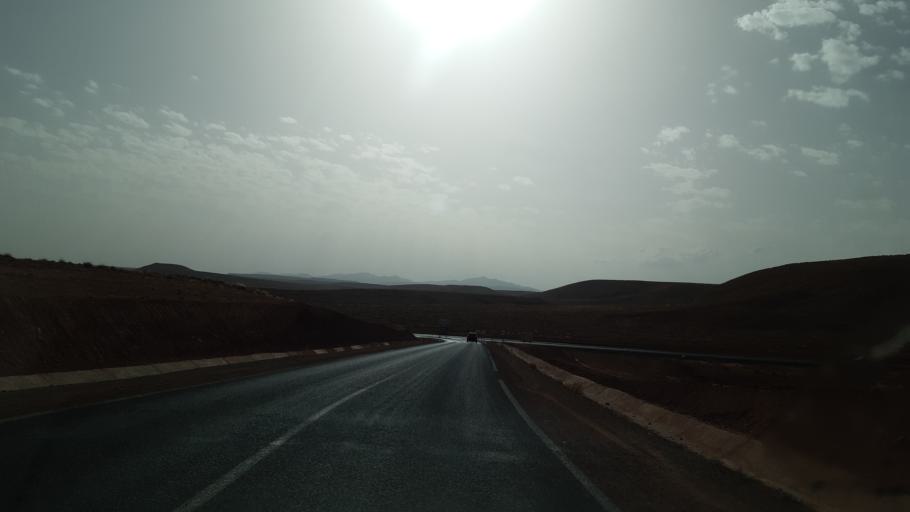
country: MA
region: Meknes-Tafilalet
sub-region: Khenifra
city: Itzer
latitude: 32.8623
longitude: -4.9429
